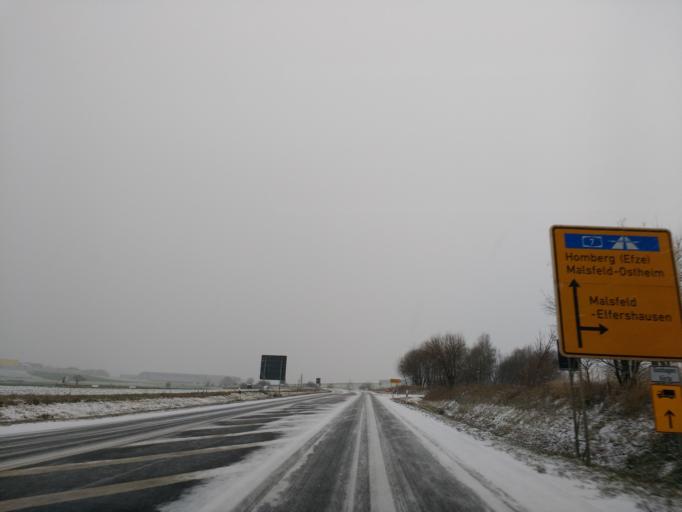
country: DE
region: Hesse
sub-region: Regierungsbezirk Kassel
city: Malsfeld
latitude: 51.0889
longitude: 9.5068
